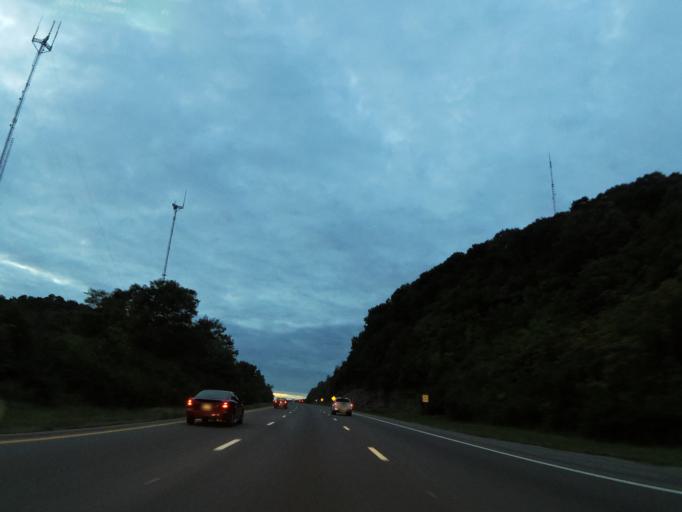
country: US
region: Tennessee
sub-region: Davidson County
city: Nashville
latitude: 36.2611
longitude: -86.7887
